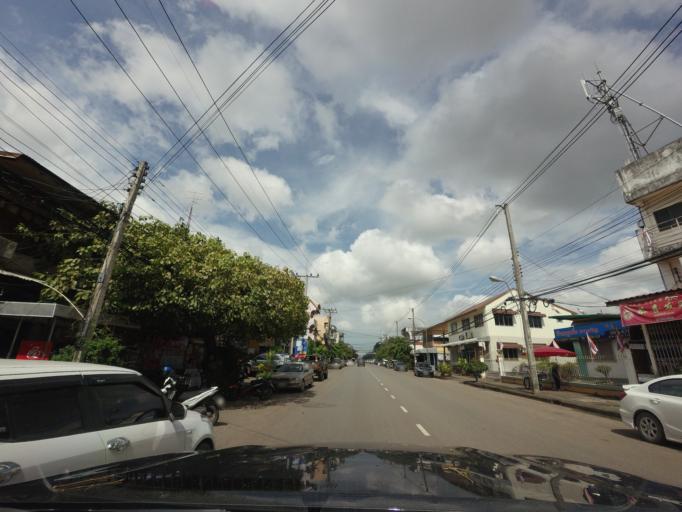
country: TH
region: Changwat Udon Thani
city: Udon Thani
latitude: 17.4021
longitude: 102.7867
